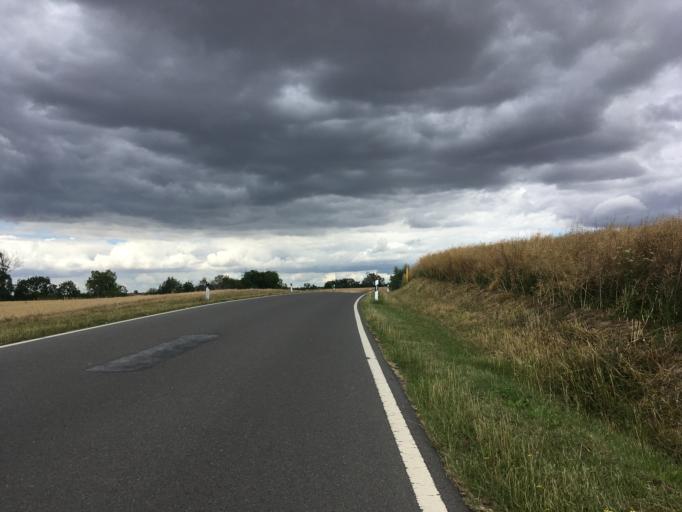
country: DE
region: Brandenburg
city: Gramzow
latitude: 53.2247
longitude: 13.9388
